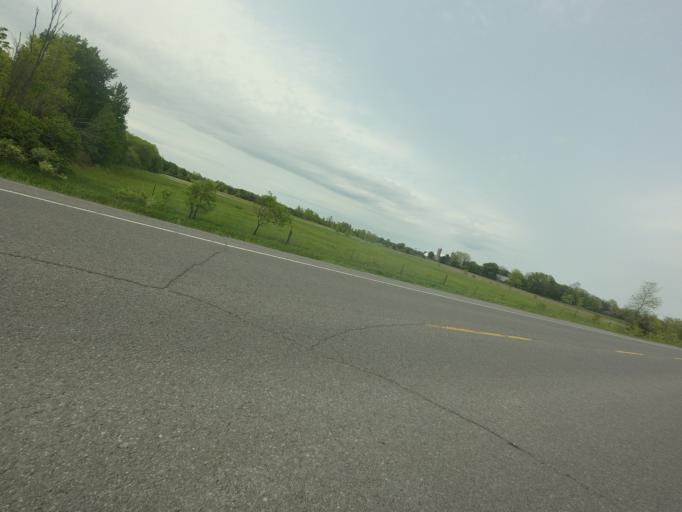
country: CA
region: Ontario
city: Kingston
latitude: 44.3178
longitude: -76.5860
